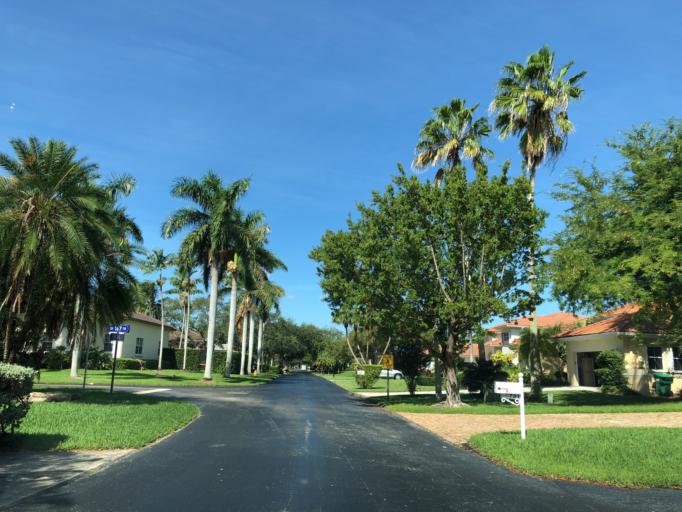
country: US
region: Florida
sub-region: Miami-Dade County
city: Palmetto Bay
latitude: 25.6150
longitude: -80.3293
